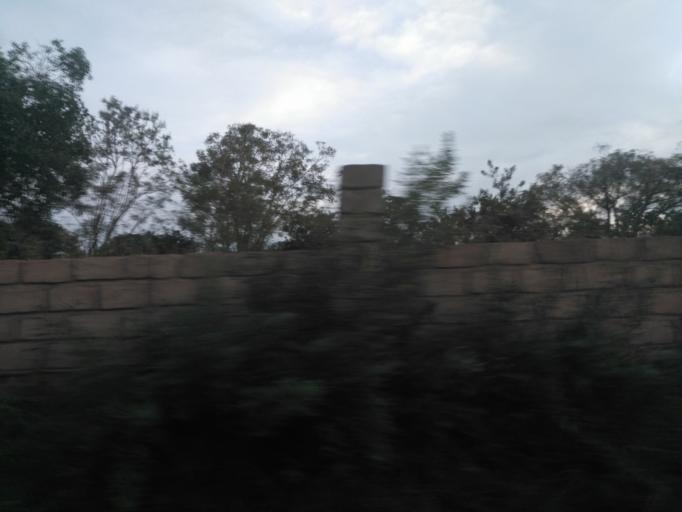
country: UG
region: Eastern Region
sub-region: Jinja District
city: Jinja
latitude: 0.4264
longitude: 33.1984
